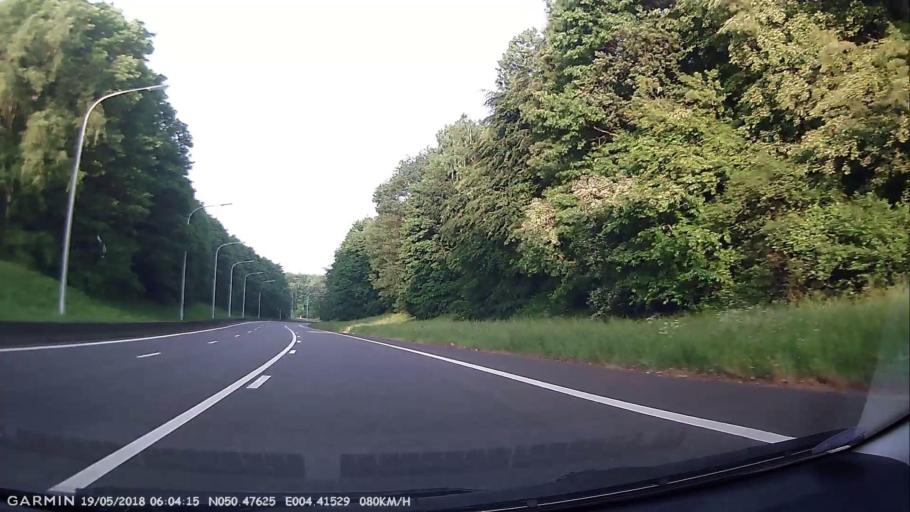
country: BE
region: Wallonia
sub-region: Province du Hainaut
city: Brunehault
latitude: 50.4760
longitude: 4.4149
